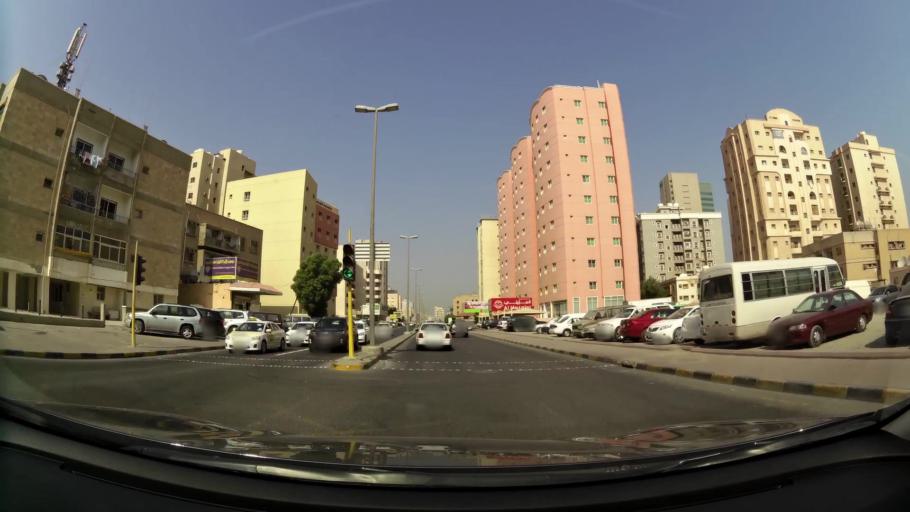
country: KW
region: Muhafazat Hawalli
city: Hawalli
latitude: 29.3373
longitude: 48.0292
